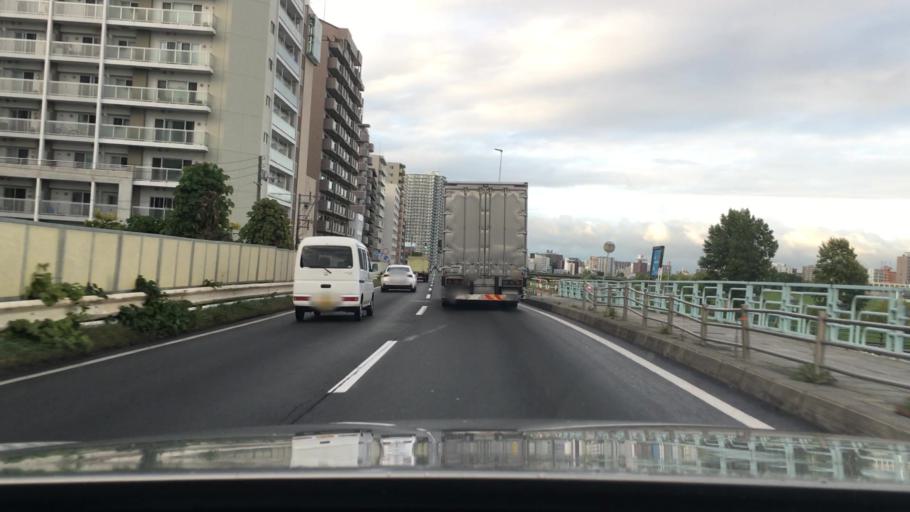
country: JP
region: Hokkaido
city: Sapporo
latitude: 43.0416
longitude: 141.3577
